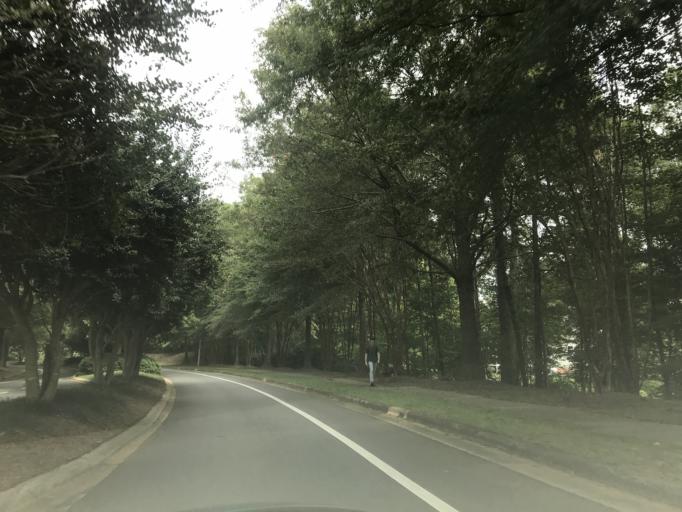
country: US
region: North Carolina
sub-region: Wake County
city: Cary
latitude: 35.7320
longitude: -78.7834
